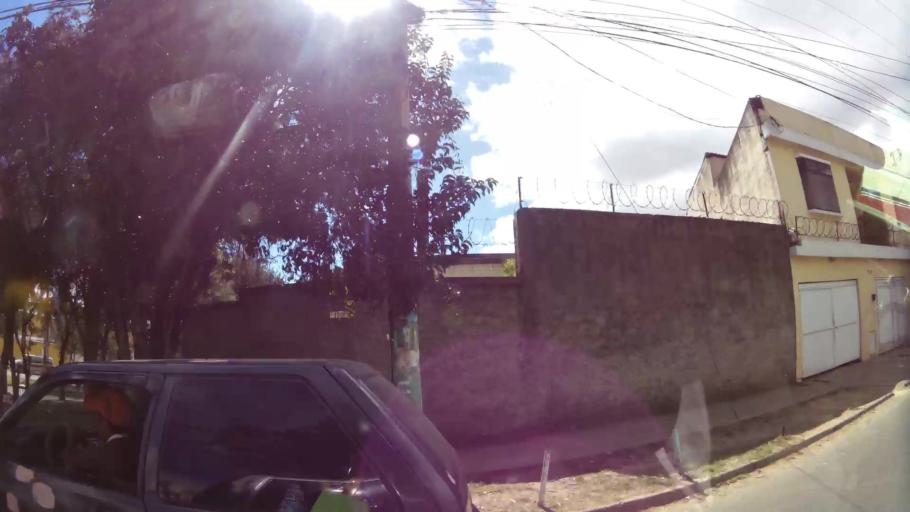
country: GT
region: Guatemala
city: Guatemala City
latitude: 14.6389
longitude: -90.5560
